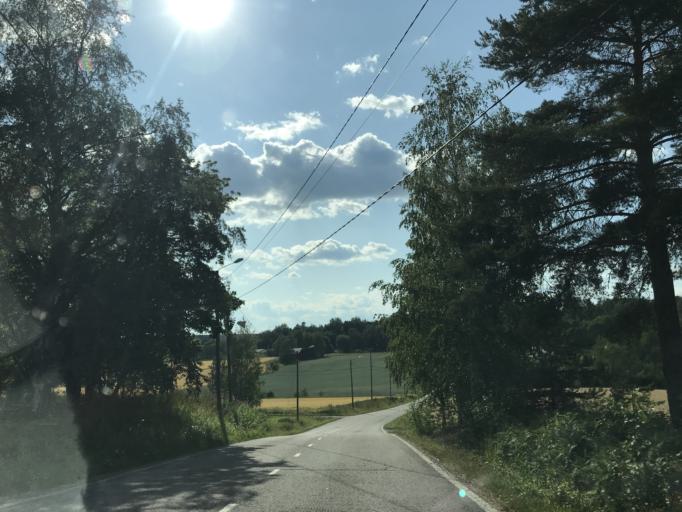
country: FI
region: Uusimaa
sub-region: Helsinki
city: Nurmijaervi
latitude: 60.4537
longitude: 24.6106
